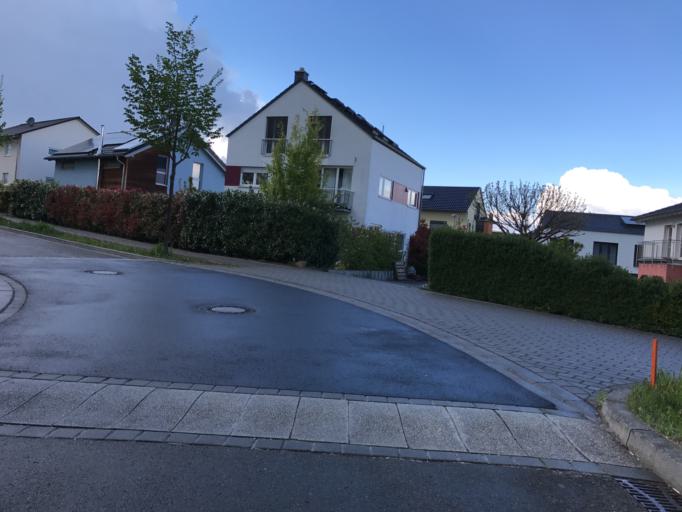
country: DE
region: Rheinland-Pfalz
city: Mainz
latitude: 50.0069
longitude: 8.2293
